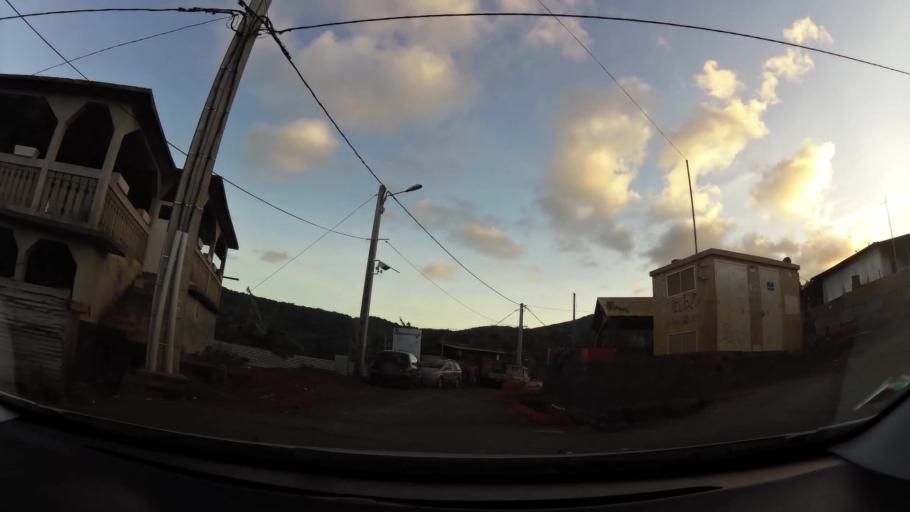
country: YT
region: Dembeni
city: Dembeni
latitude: -12.8678
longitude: 45.1957
